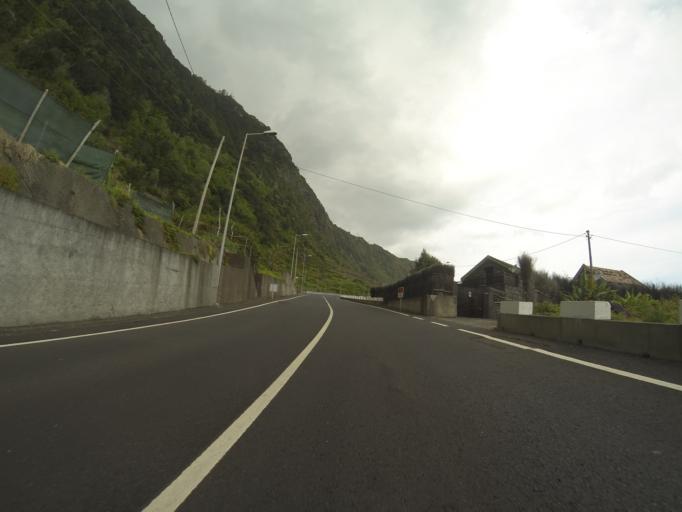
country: PT
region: Madeira
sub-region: Porto Moniz
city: Porto Moniz
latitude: 32.8443
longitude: -17.1448
